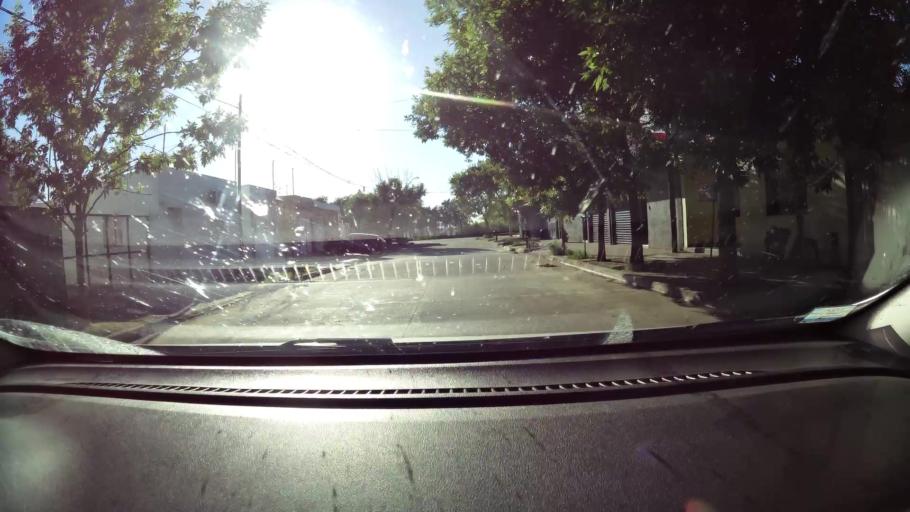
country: AR
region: Cordoba
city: San Francisco
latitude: -31.4433
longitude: -62.0997
